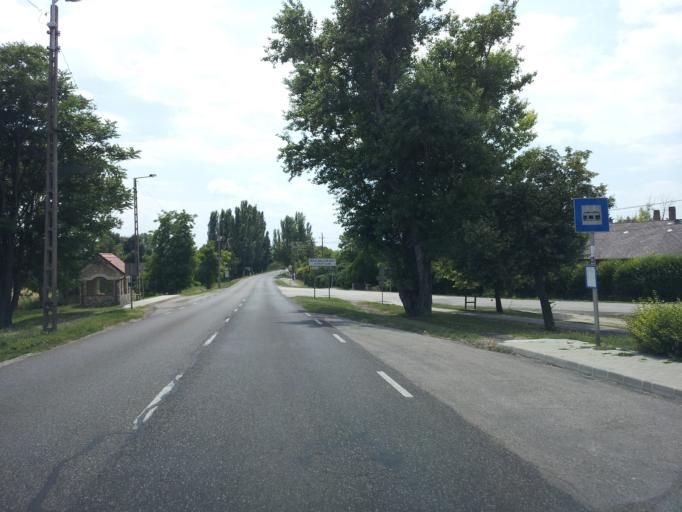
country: HU
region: Veszprem
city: Tihany
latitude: 46.9131
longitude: 17.8162
